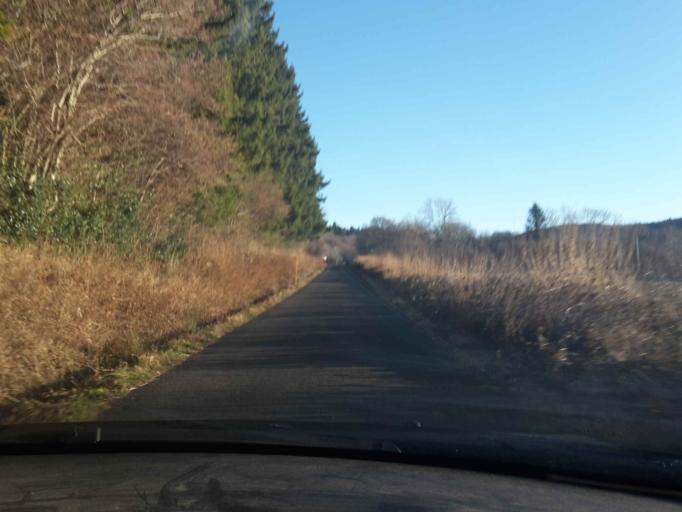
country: FR
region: Auvergne
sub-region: Departement du Cantal
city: Riom-es-Montagnes
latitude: 45.2317
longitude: 2.5604
